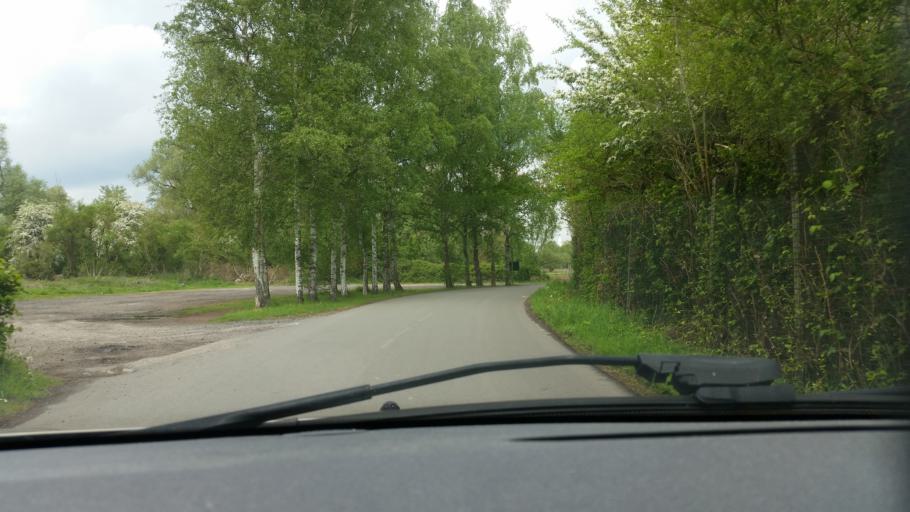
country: FR
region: Nord-Pas-de-Calais
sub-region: Departement du Pas-de-Calais
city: Billy-Berclau
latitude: 50.5102
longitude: 2.8707
